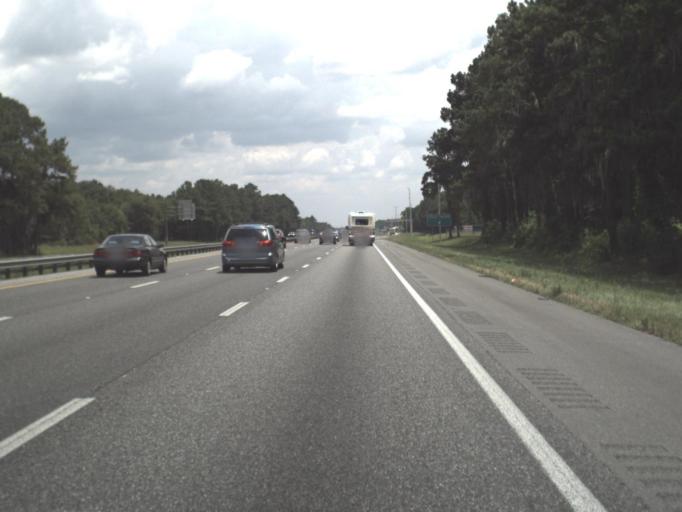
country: US
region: Florida
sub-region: Hamilton County
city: Jasper
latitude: 30.4321
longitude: -82.9110
